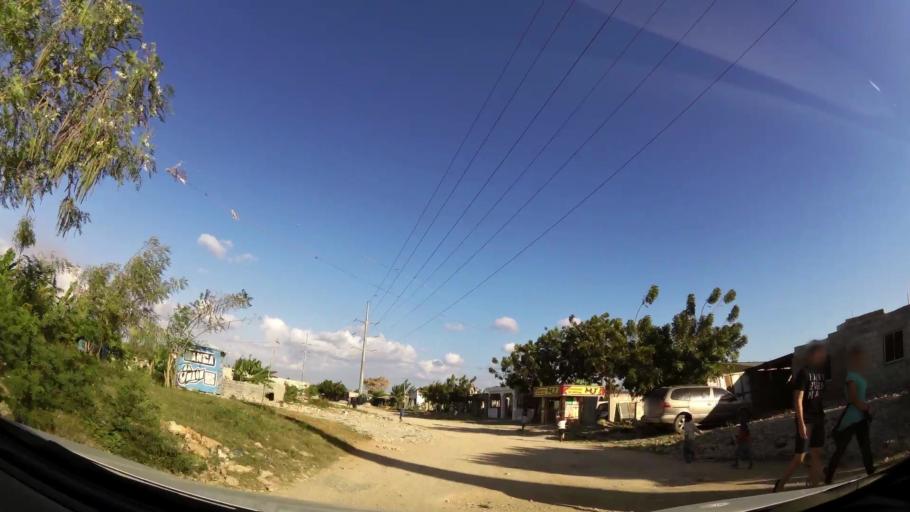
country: DO
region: Santo Domingo
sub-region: Santo Domingo
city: Santo Domingo Este
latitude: 18.4762
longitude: -69.8136
